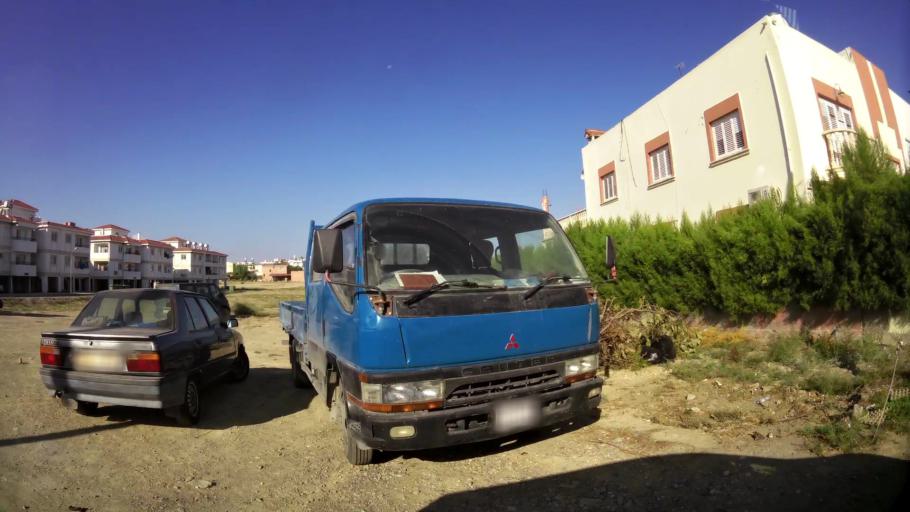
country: CY
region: Lefkosia
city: Nicosia
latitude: 35.2138
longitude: 33.3014
